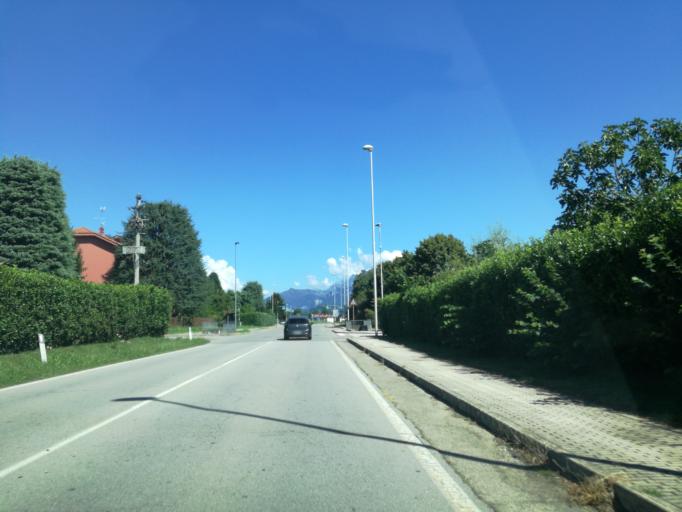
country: IT
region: Lombardy
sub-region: Provincia di Lecco
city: Imbersago
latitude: 45.7047
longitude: 9.4494
